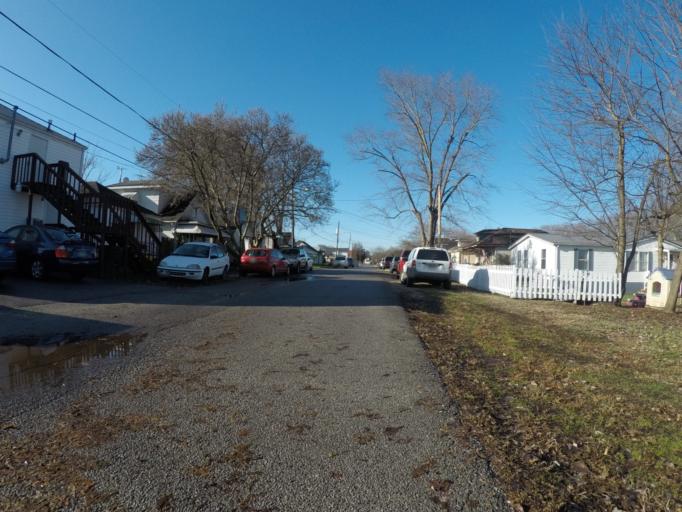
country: US
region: West Virginia
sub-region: Cabell County
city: Huntington
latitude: 38.4120
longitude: -82.4880
